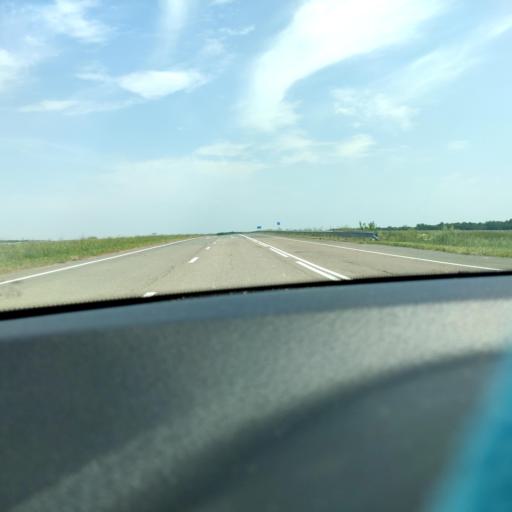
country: RU
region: Samara
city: Petra-Dubrava
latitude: 53.3395
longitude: 50.4467
